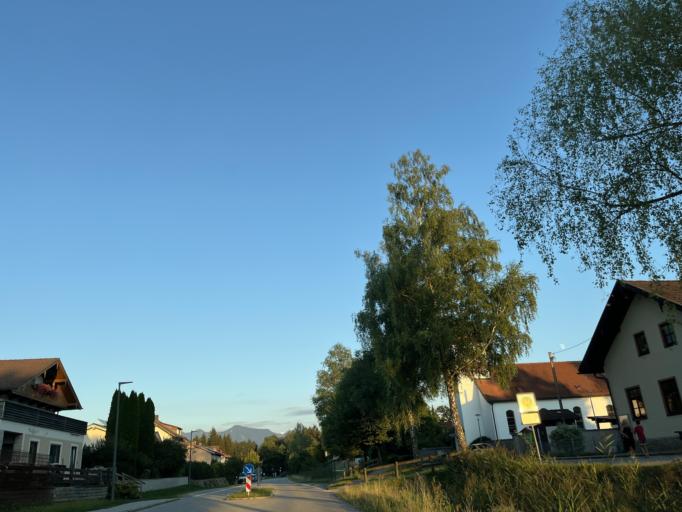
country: DE
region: Bavaria
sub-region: Upper Bavaria
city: Raubling
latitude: 47.7894
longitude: 12.0791
